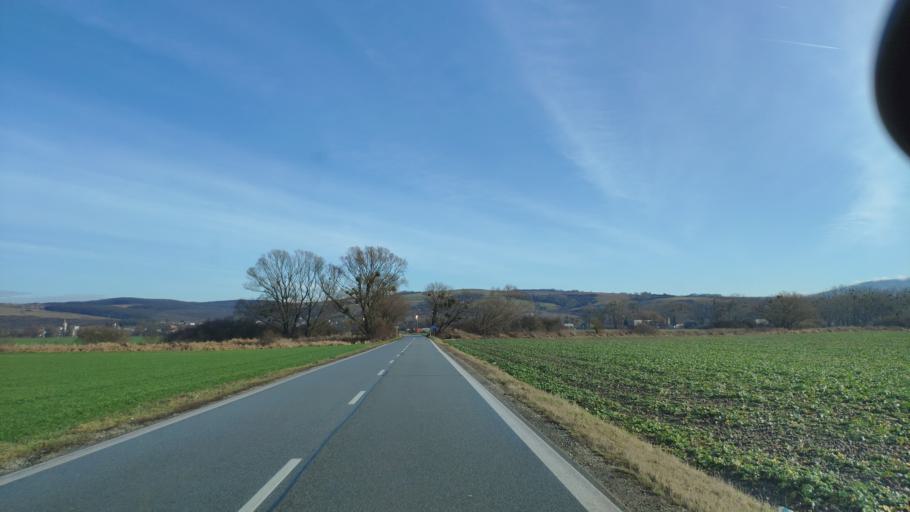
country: SK
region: Kosicky
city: Kosice
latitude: 48.6867
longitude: 21.3291
